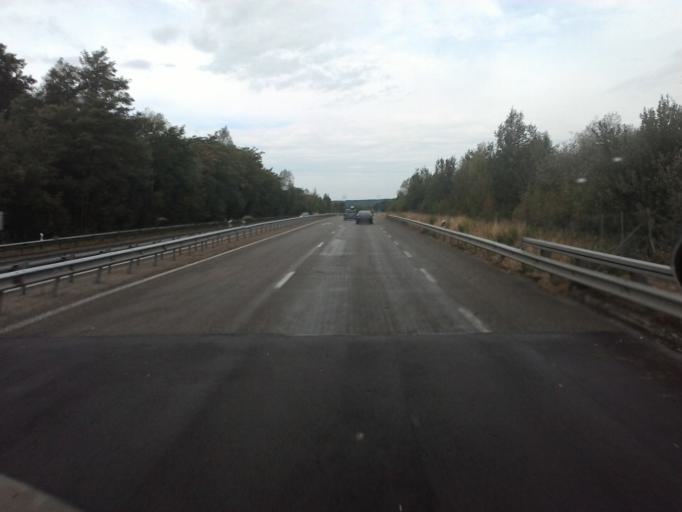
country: FR
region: Franche-Comte
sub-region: Departement du Jura
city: Poligny
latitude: 46.8426
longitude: 5.6598
